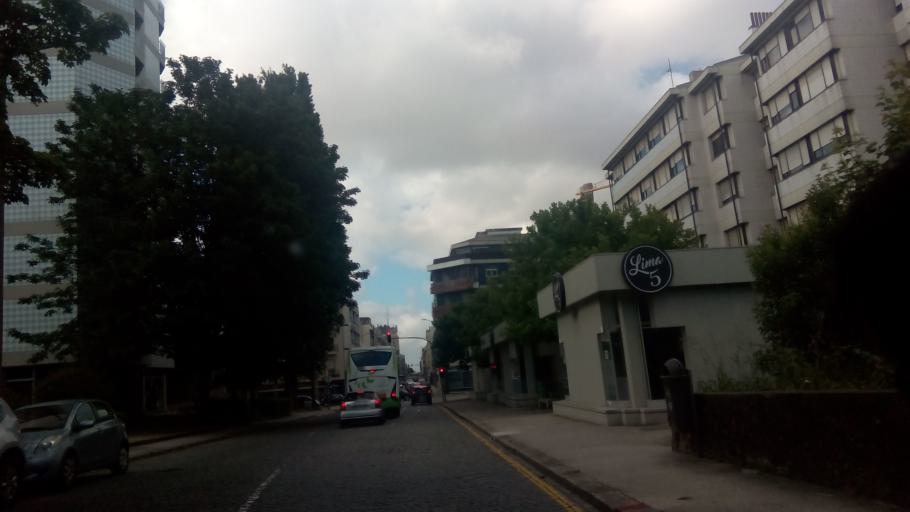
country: PT
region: Porto
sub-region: Porto
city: Porto
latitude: 41.1622
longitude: -8.6000
